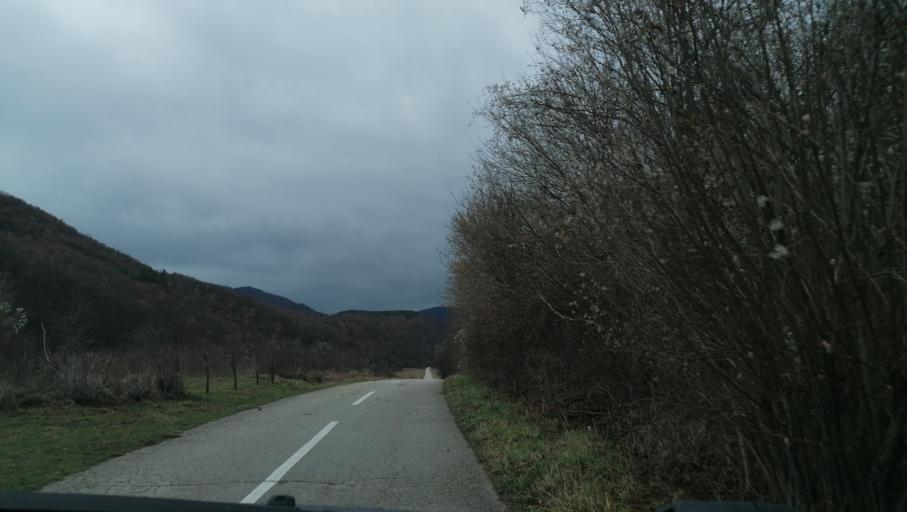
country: RS
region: Central Serbia
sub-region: Pirotski Okrug
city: Dimitrovgrad
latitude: 42.9349
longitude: 22.7721
